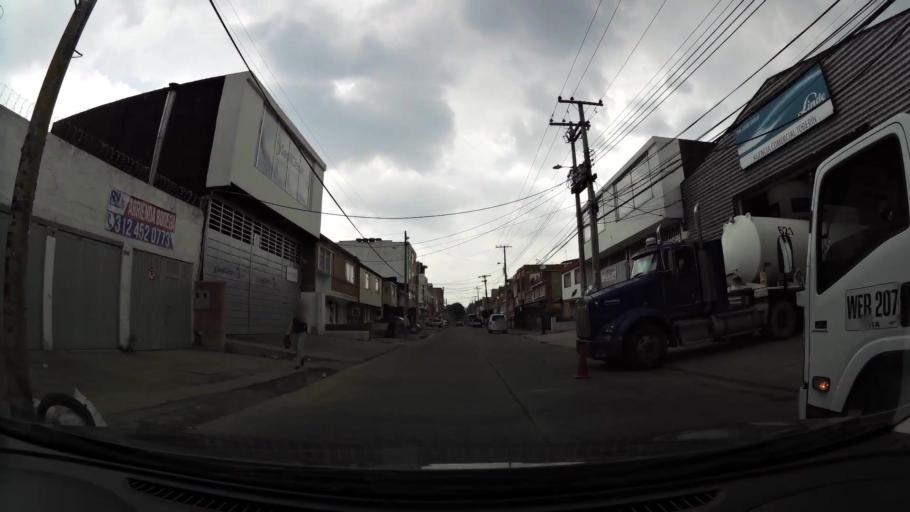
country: CO
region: Cundinamarca
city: La Calera
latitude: 4.7434
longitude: -74.0431
